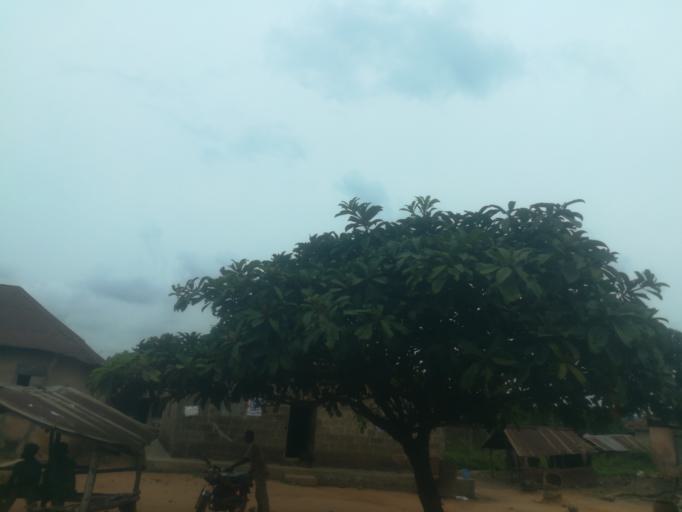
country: NG
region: Ogun
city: Ayetoro
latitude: 7.1120
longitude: 3.1229
